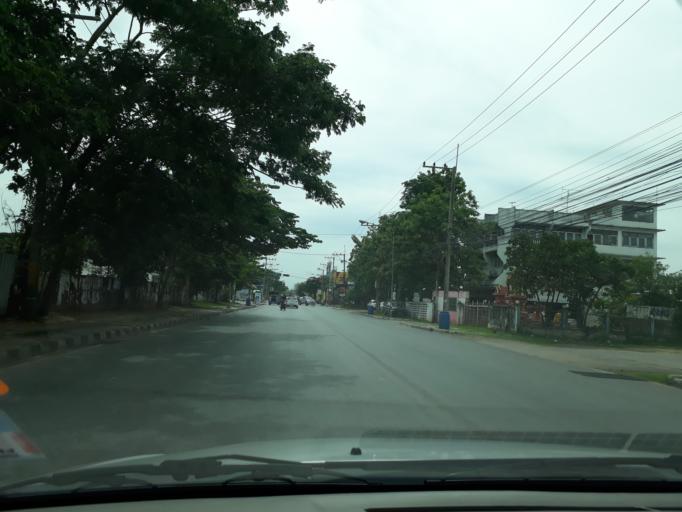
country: TH
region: Khon Kaen
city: Khon Kaen
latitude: 16.4370
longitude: 102.8451
